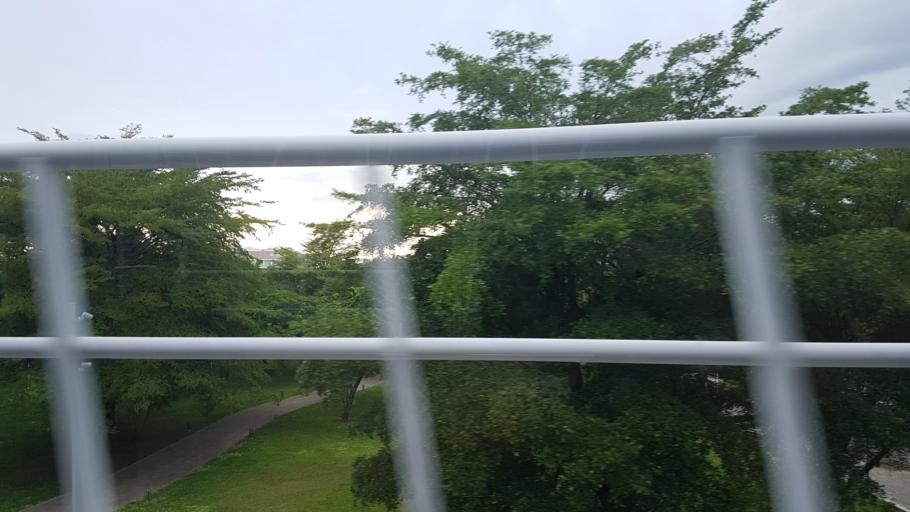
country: TW
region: Kaohsiung
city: Kaohsiung
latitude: 22.6186
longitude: 120.2884
